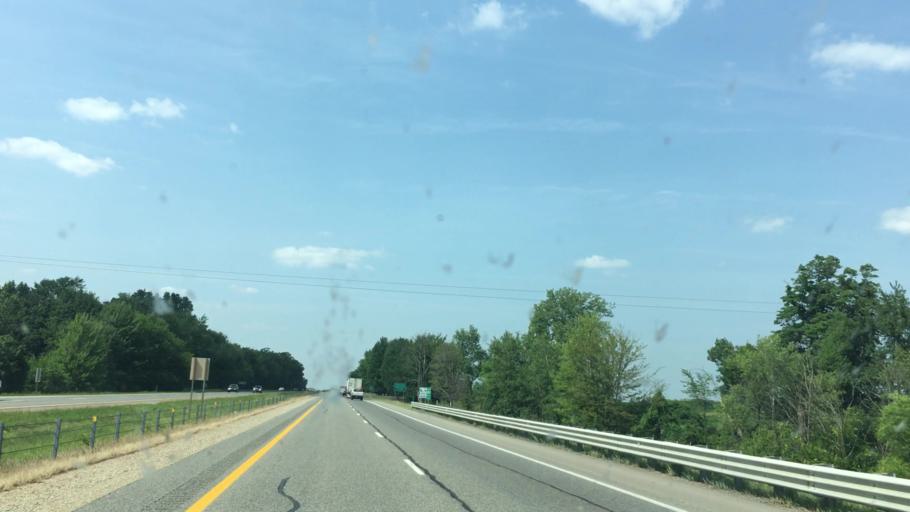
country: US
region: Michigan
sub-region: Allegan County
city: Otsego
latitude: 42.5222
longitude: -85.6571
